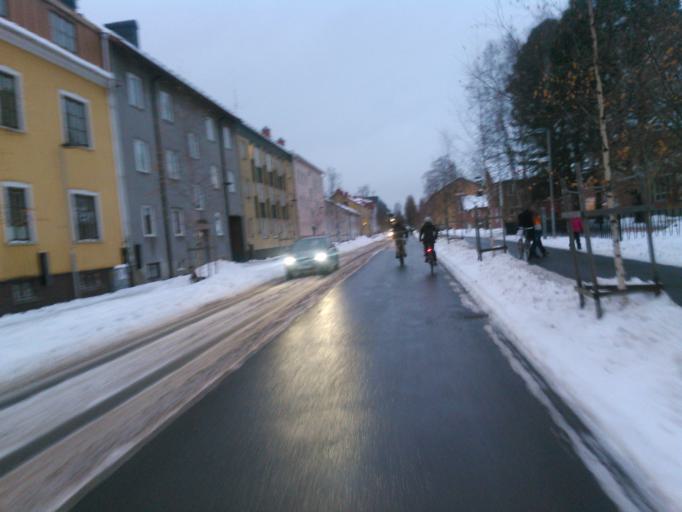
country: SE
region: Vaesterbotten
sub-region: Umea Kommun
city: Umea
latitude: 63.8256
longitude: 20.2763
